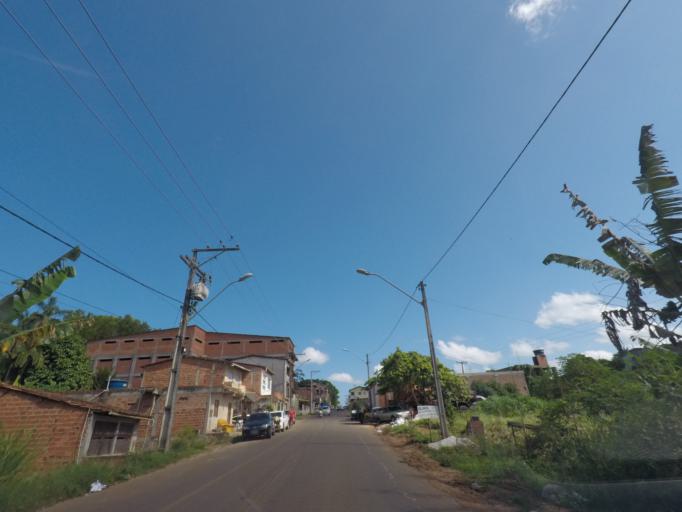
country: BR
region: Bahia
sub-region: Camamu
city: Camamu
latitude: -13.9386
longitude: -39.1060
